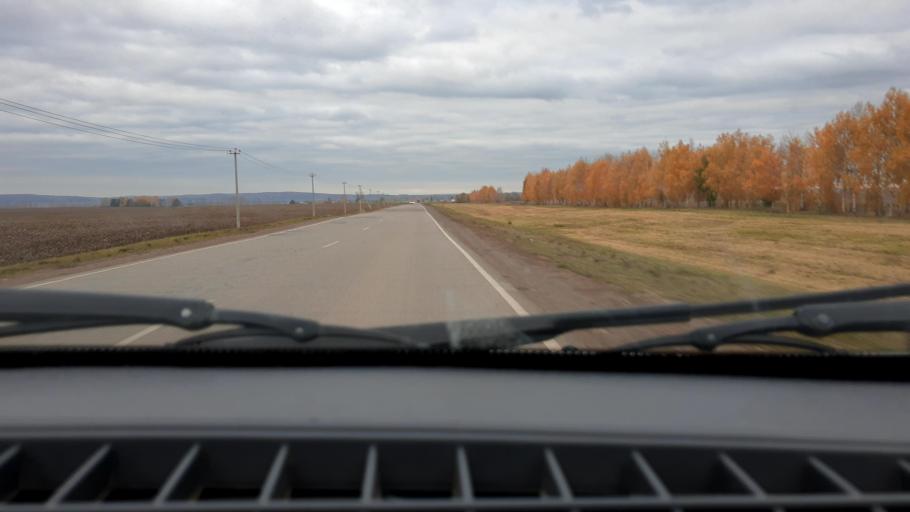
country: RU
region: Bashkortostan
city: Kabakovo
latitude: 54.5405
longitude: 56.0770
